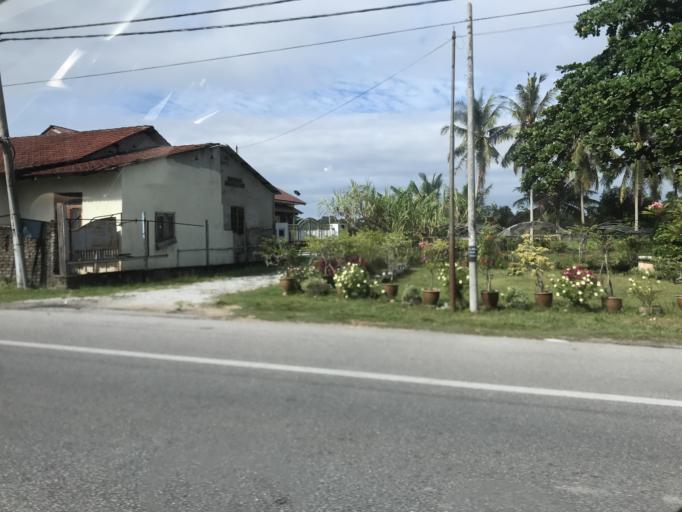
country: MY
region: Kelantan
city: Kota Bharu
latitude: 6.1240
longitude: 102.1833
